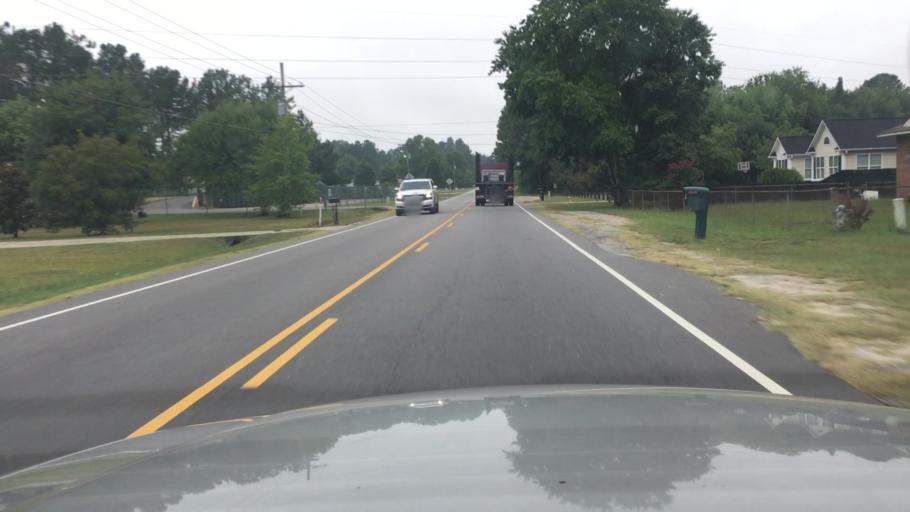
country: US
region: North Carolina
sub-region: Hoke County
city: Rockfish
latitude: 34.9717
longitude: -79.0144
